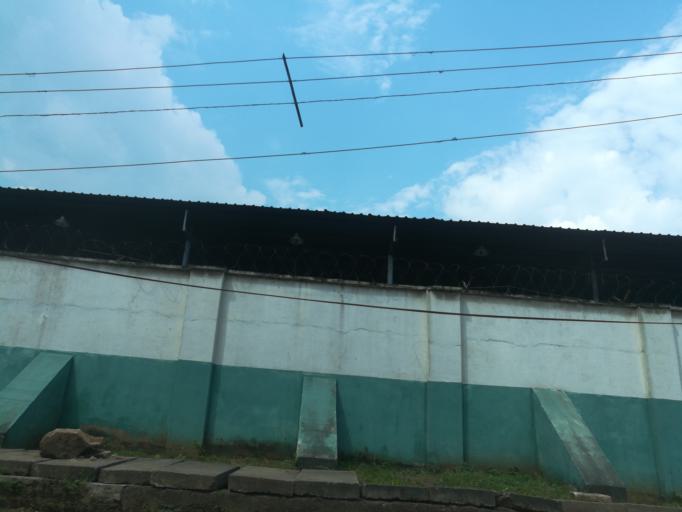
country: NG
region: Lagos
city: Ikeja
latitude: 6.6070
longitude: 3.3638
